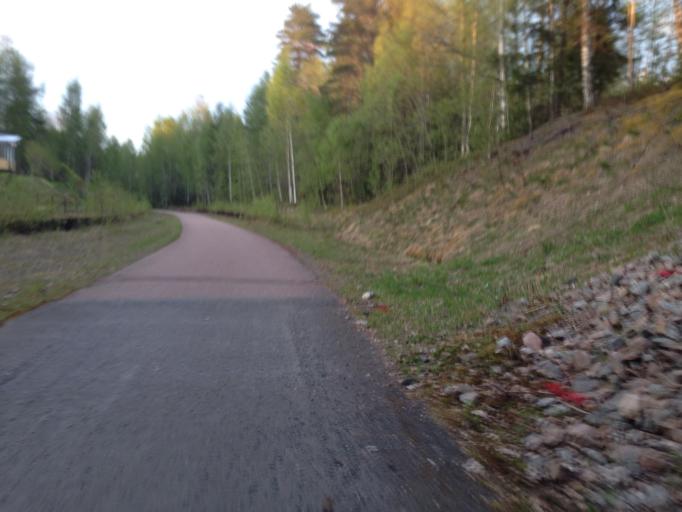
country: SE
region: Dalarna
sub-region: Ludvika Kommun
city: Grangesberg
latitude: 60.1245
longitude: 15.0685
